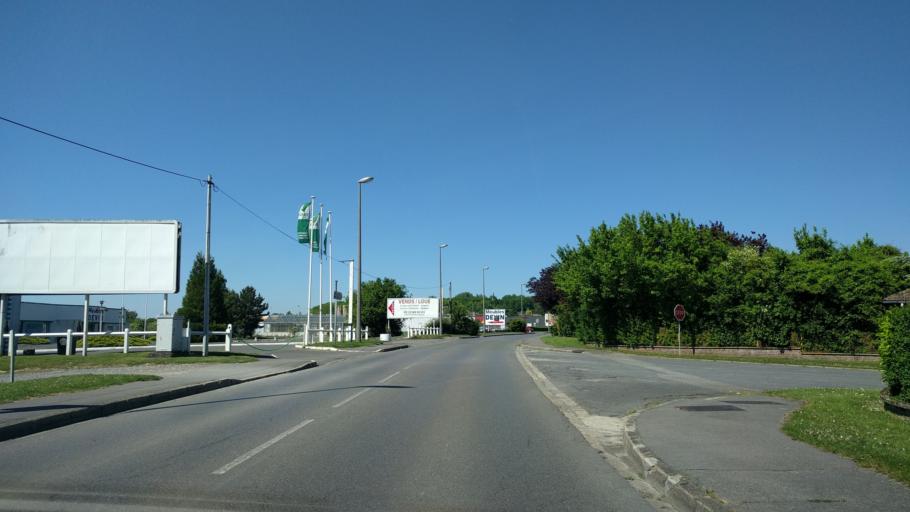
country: FR
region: Picardie
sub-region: Departement de la Somme
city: Peronne
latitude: 49.9386
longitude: 2.9316
